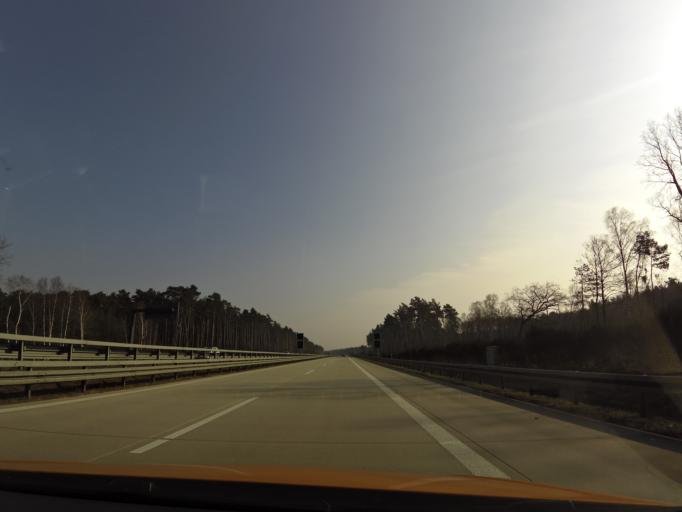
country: DE
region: Brandenburg
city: Briesen
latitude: 52.3269
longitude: 14.2766
